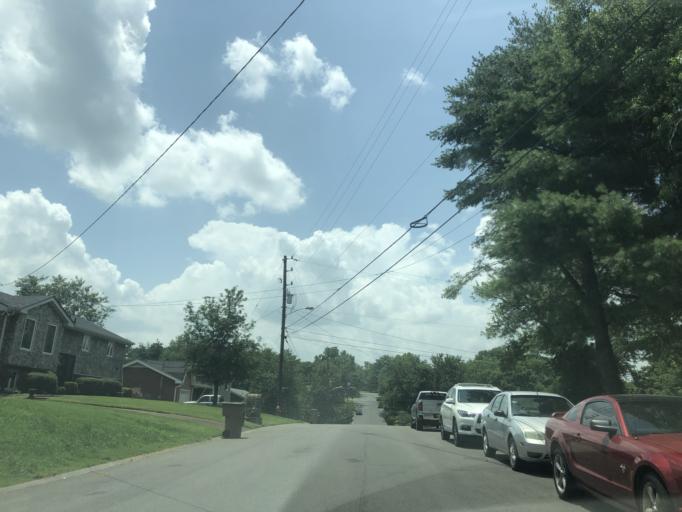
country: US
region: Tennessee
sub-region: Williamson County
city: Brentwood Estates
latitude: 36.0487
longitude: -86.6920
